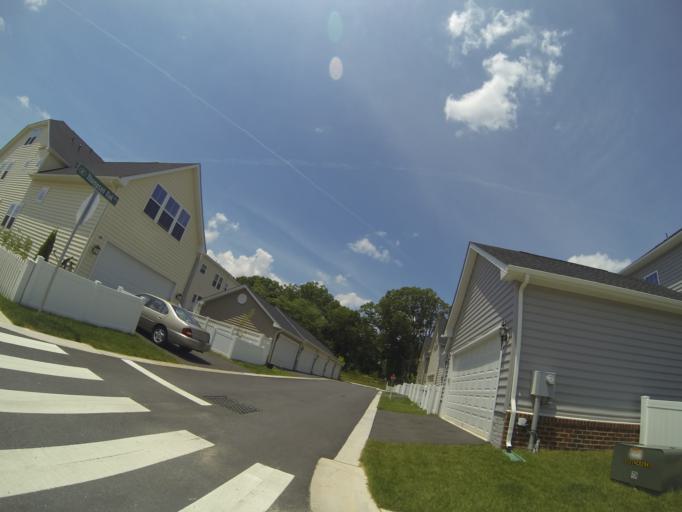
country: US
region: Maryland
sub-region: Montgomery County
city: Clarksburg
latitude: 39.2238
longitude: -77.2459
